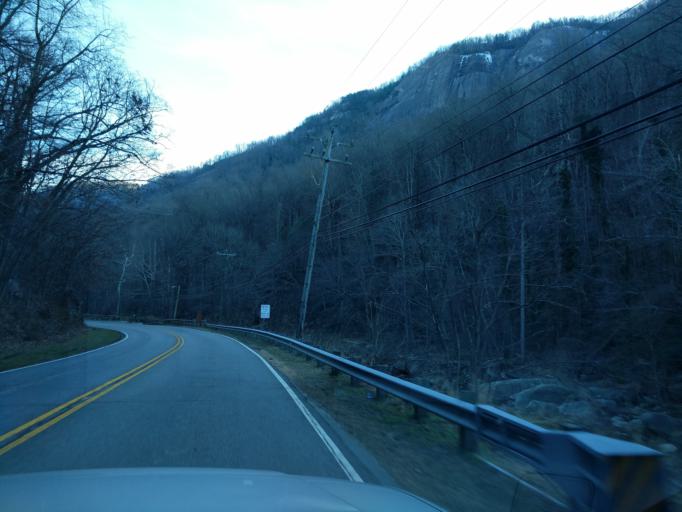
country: US
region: North Carolina
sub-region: Rutherford County
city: Lake Lure
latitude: 35.4466
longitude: -82.2756
